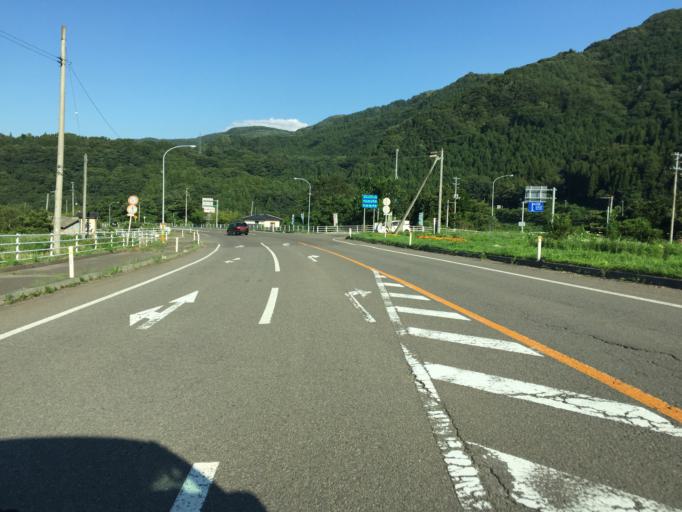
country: JP
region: Miyagi
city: Shiroishi
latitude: 37.9459
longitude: 140.5400
